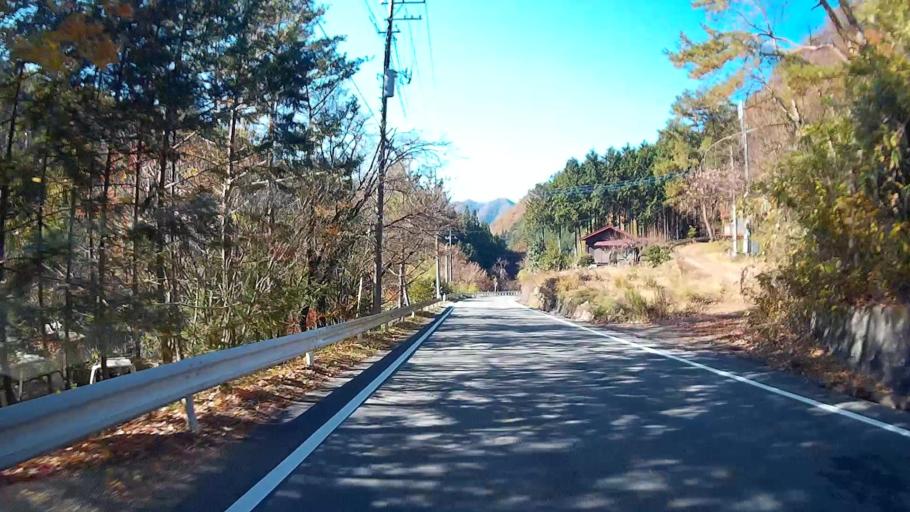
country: JP
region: Yamanashi
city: Otsuki
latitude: 35.5634
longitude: 139.0014
